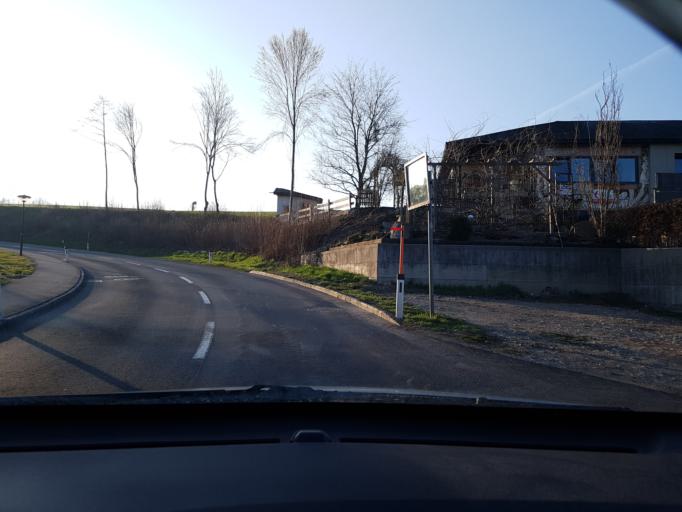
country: AT
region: Upper Austria
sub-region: Politischer Bezirk Linz-Land
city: Sankt Florian
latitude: 48.1648
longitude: 14.3354
